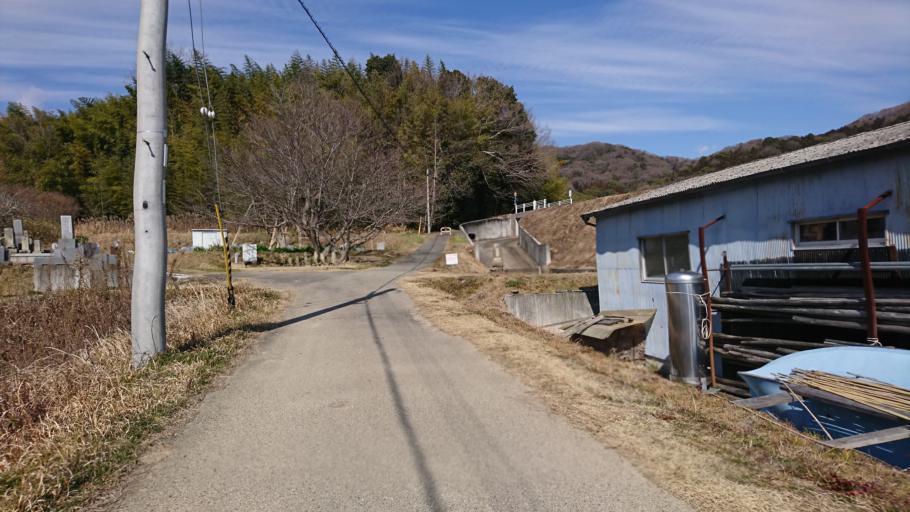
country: JP
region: Hyogo
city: Kakogawacho-honmachi
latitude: 34.8269
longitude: 134.8086
